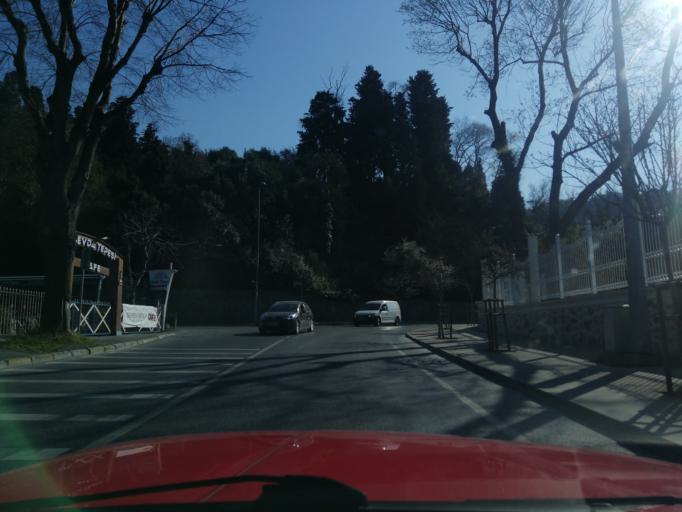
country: TR
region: Istanbul
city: UEskuedar
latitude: 41.0764
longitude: 29.0662
